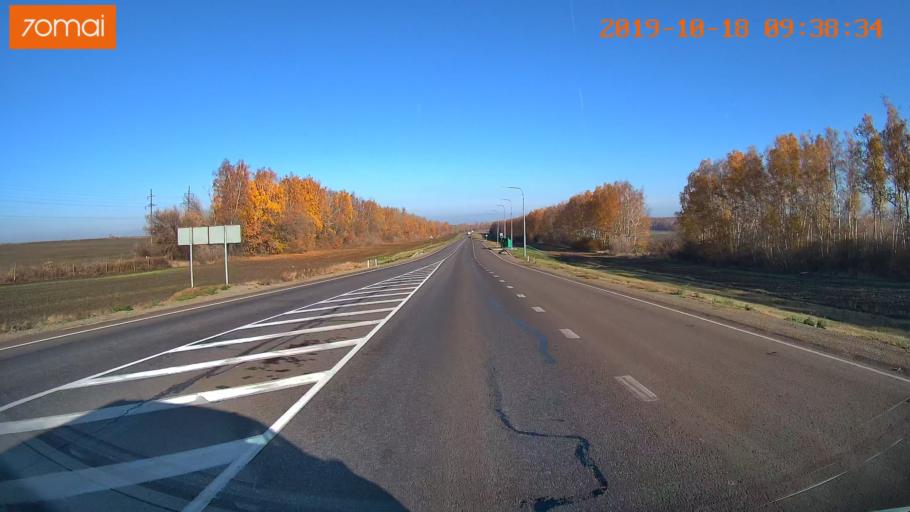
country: RU
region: Tula
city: Yefremov
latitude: 53.2398
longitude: 38.1366
